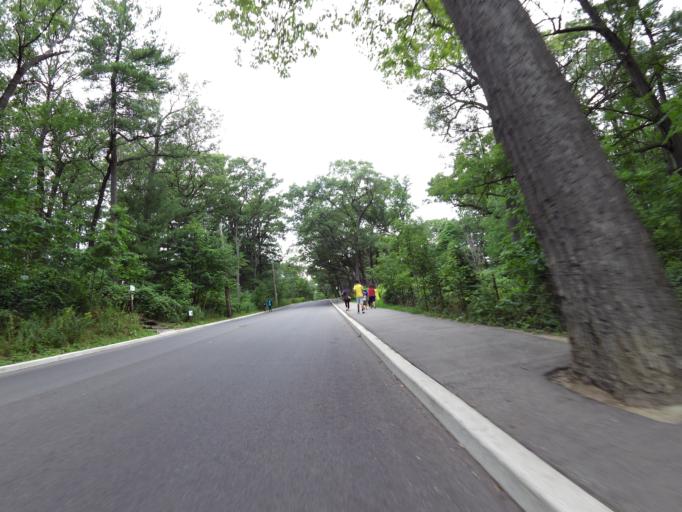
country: CA
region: Ontario
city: Toronto
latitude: 43.6452
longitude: -79.4600
